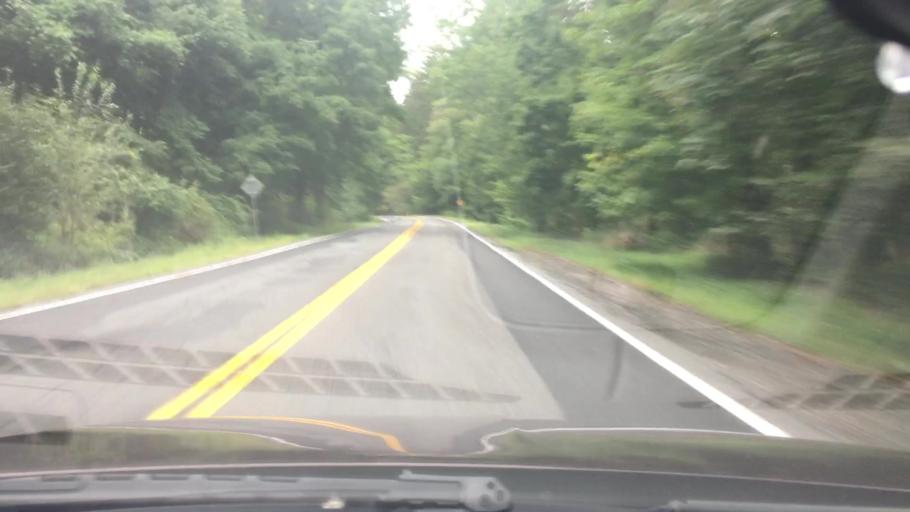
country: US
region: New York
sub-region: Dutchess County
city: Millbrook
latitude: 41.7922
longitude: -73.6870
